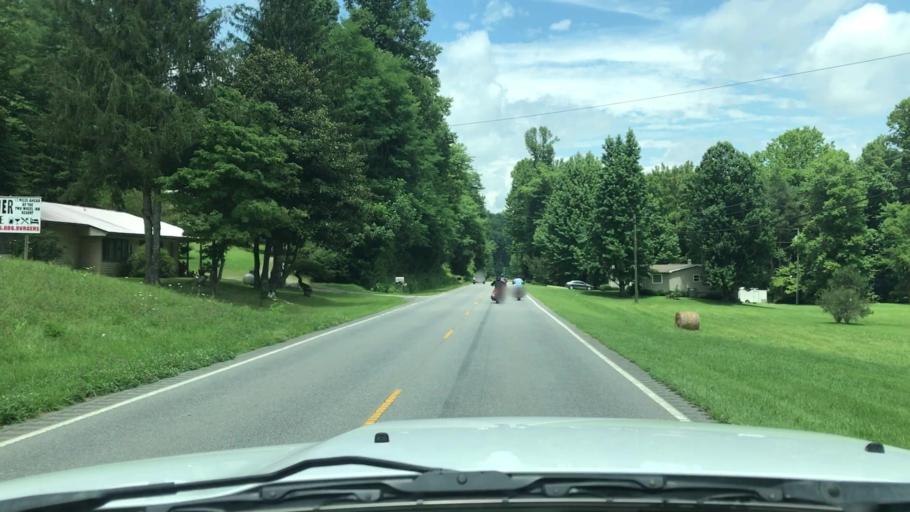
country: US
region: North Carolina
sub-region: Graham County
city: Robbinsville
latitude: 35.2792
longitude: -83.7630
